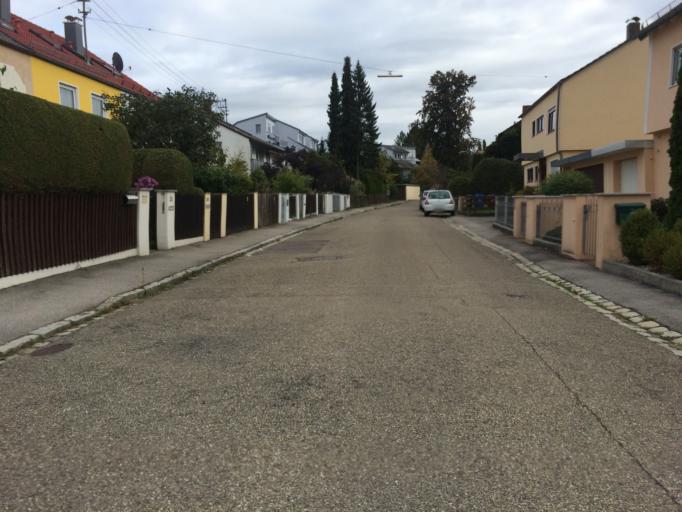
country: DE
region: Bavaria
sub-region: Swabia
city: Friedberg
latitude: 48.3499
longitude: 10.9903
